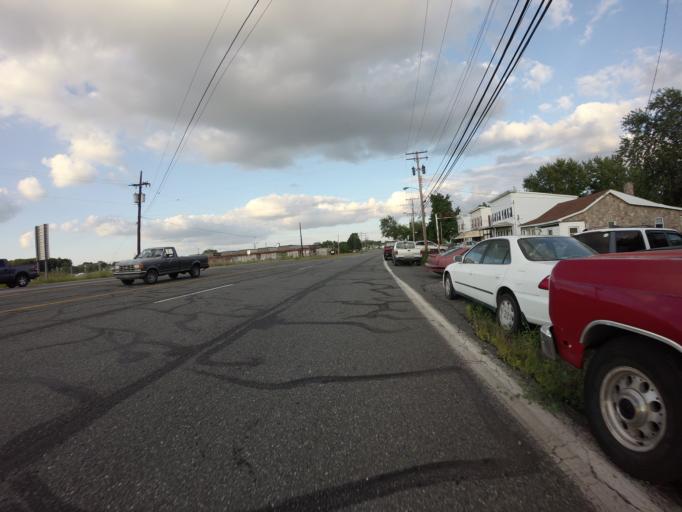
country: US
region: Maryland
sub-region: Baltimore County
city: Edgemere
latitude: 39.2322
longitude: -76.4625
